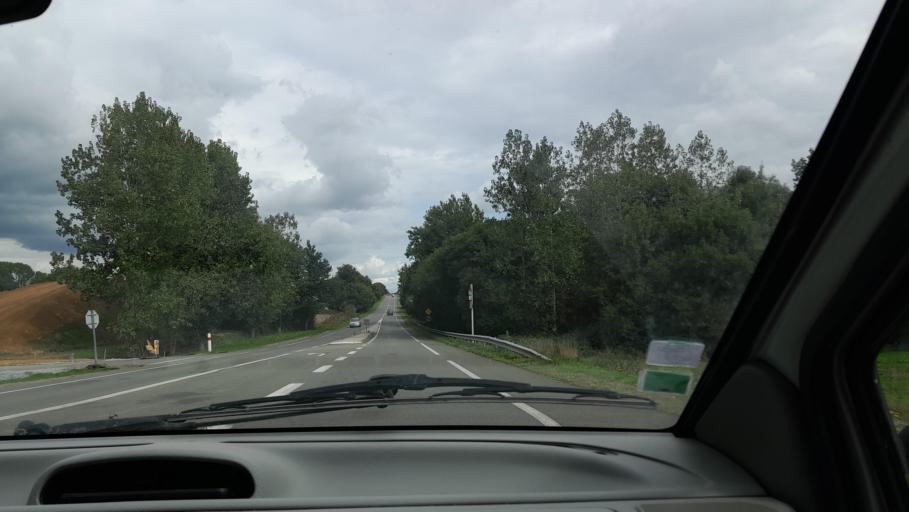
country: FR
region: Pays de la Loire
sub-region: Departement de la Mayenne
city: Ahuille
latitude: 47.9822
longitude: -0.8624
